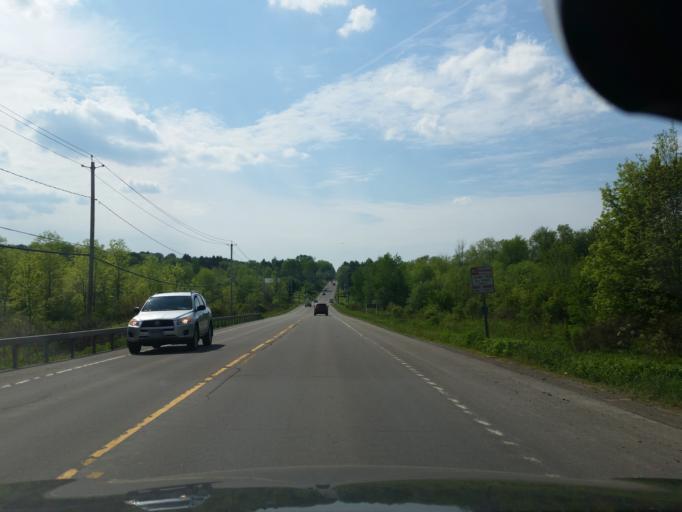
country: US
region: New York
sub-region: Chautauqua County
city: Lakewood
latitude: 42.1054
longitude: -79.3672
